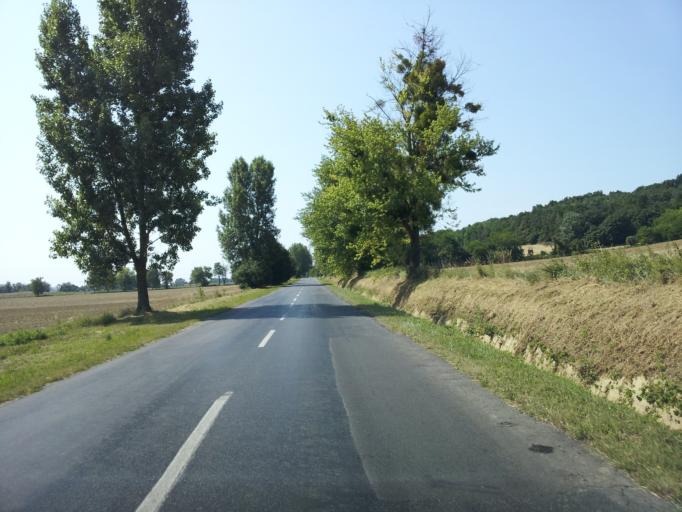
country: HU
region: Zala
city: Heviz
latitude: 46.8324
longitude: 17.0926
